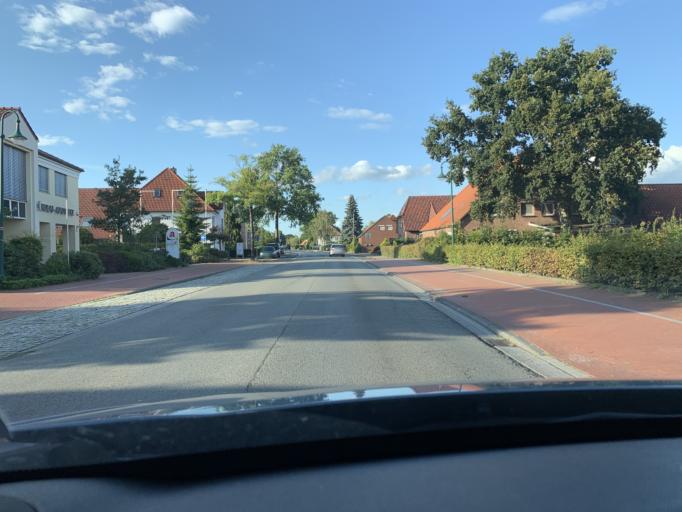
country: DE
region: Lower Saxony
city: Edewecht
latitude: 53.1324
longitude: 7.9865
